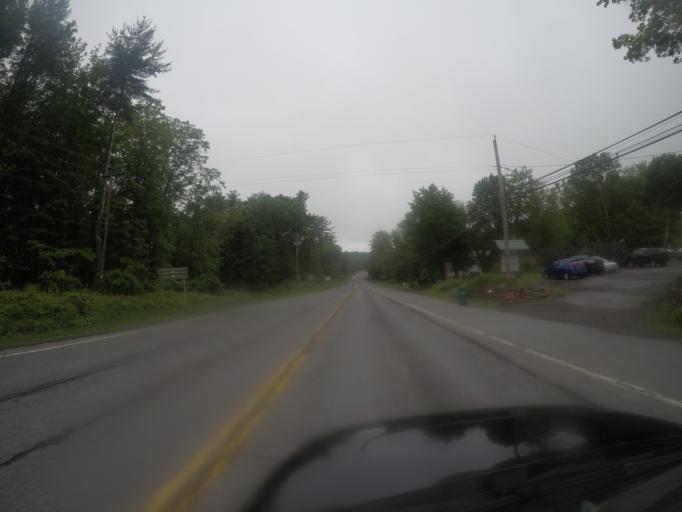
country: US
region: New York
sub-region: Ulster County
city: West Hurley
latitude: 41.9974
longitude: -74.1059
